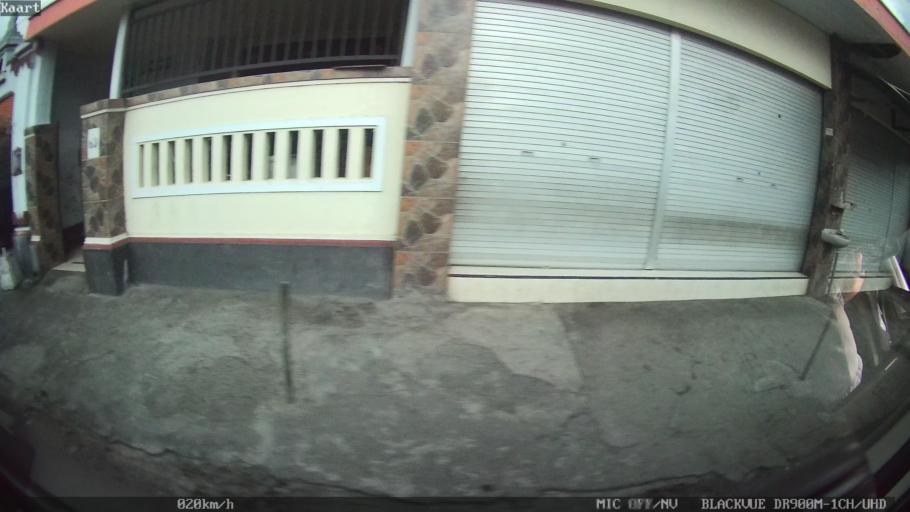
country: ID
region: Bali
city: Banjar Kertasari
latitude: -8.6196
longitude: 115.2022
